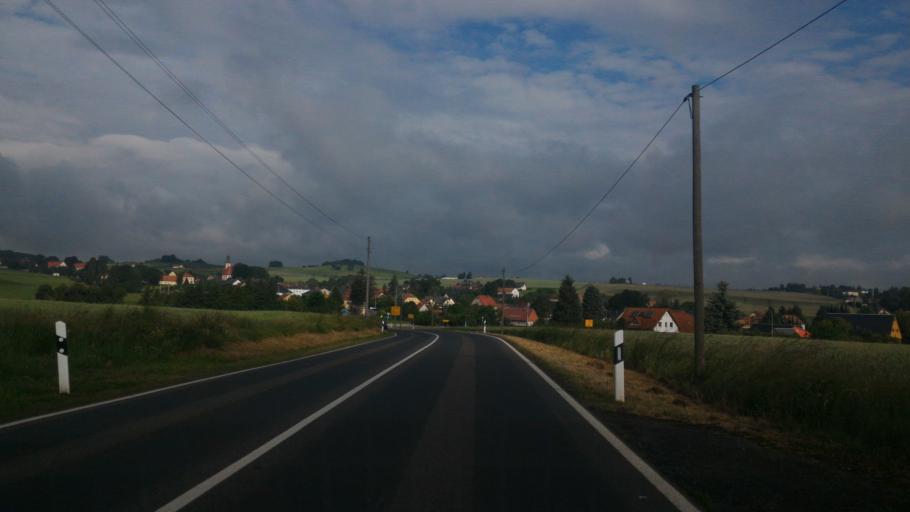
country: DE
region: Saxony
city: Hainewalde
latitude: 50.9364
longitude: 14.6917
